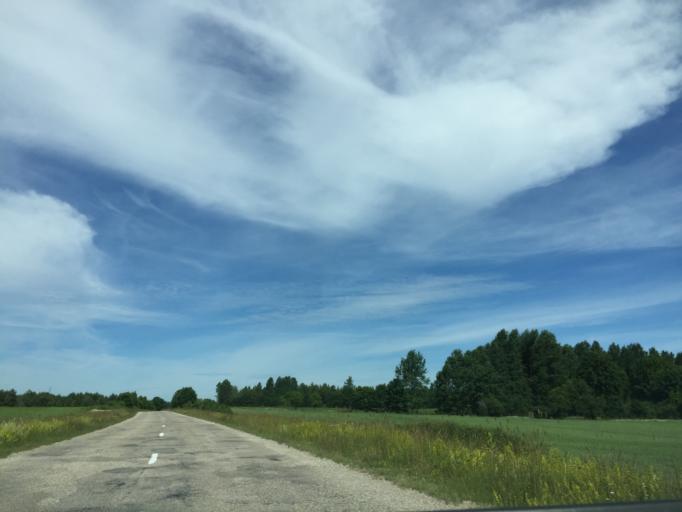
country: LV
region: Dundaga
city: Dundaga
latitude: 57.5435
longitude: 22.3258
